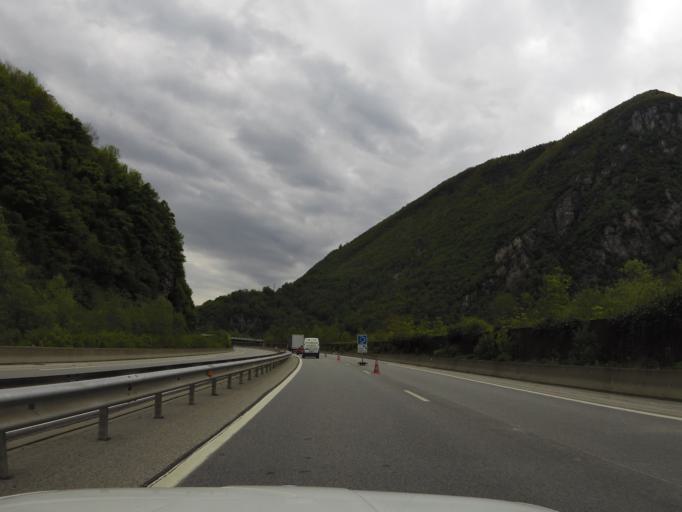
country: FR
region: Rhone-Alpes
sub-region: Departement de la Savoie
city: Saint-Remy-de-Maurienne
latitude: 45.4567
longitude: 6.2909
